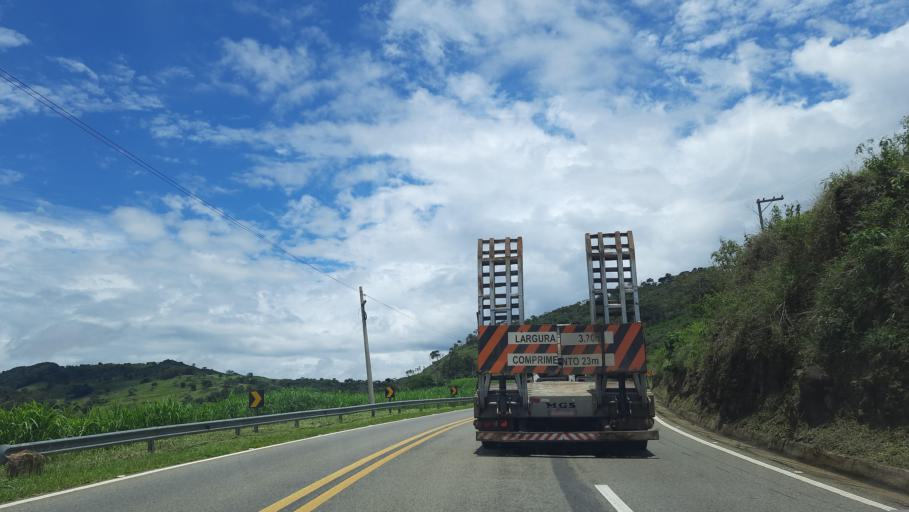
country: BR
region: Sao Paulo
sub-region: Vargem Grande Do Sul
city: Vargem Grande do Sul
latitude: -21.8317
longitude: -46.7628
